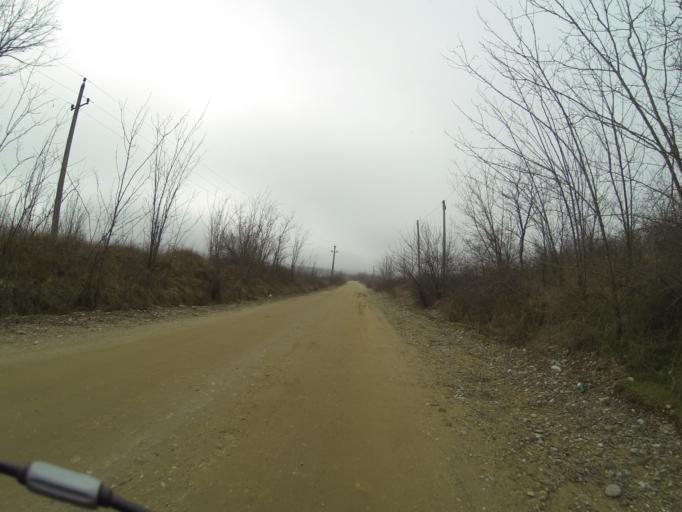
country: RO
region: Mehedinti
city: Dumbrava de Sus
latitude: 44.4875
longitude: 23.0776
